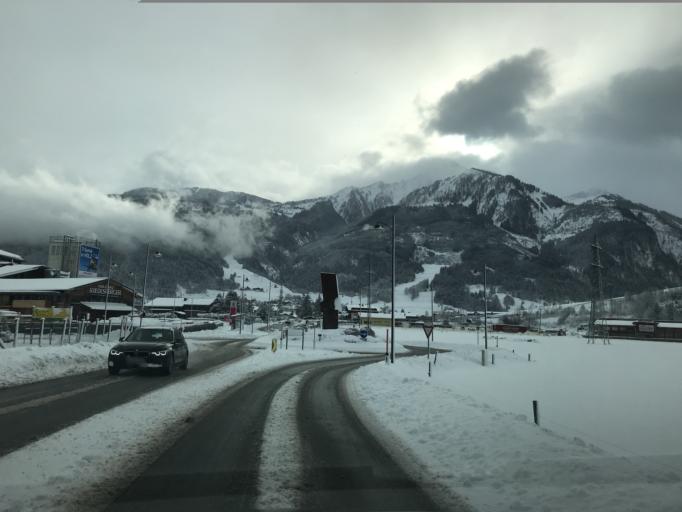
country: AT
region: Salzburg
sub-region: Politischer Bezirk Zell am See
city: Kaprun
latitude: 47.2831
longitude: 12.7531
